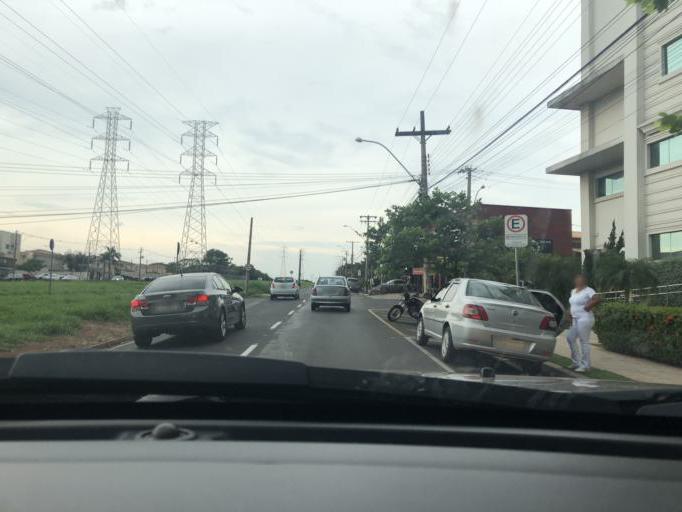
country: BR
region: Sao Paulo
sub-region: Sao Jose Do Rio Preto
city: Sao Jose do Rio Preto
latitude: -20.8445
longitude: -49.3933
